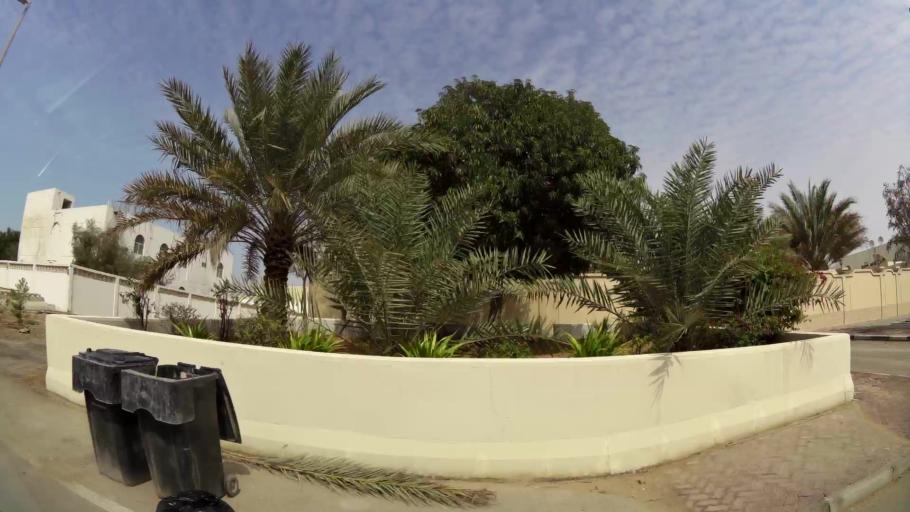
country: AE
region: Abu Dhabi
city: Abu Dhabi
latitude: 24.5205
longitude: 54.6599
